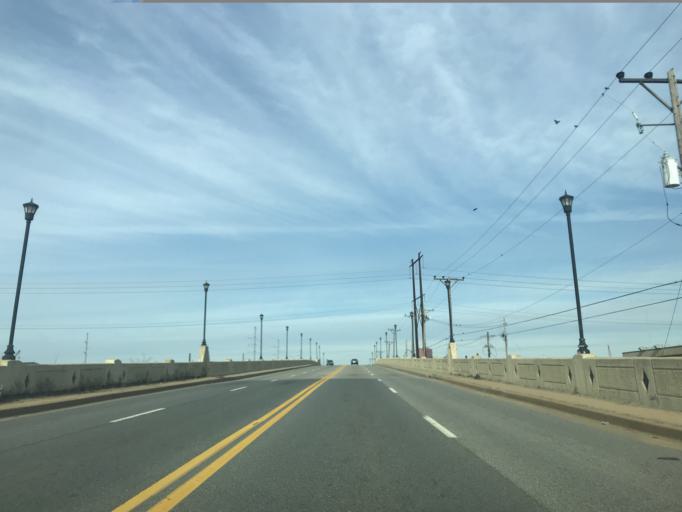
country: US
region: Delaware
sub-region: New Castle County
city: Wilmington
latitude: 39.7228
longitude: -75.5557
